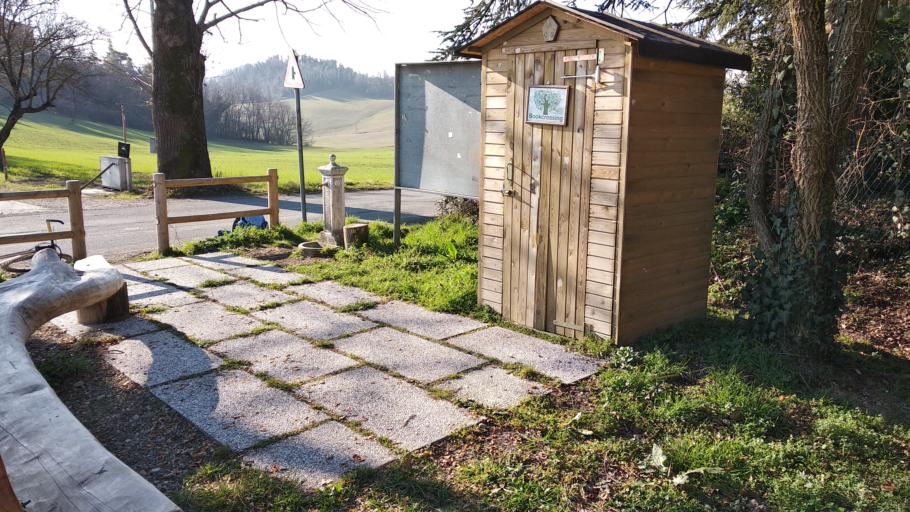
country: IT
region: Emilia-Romagna
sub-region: Provincia di Bologna
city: Ozzano dell'Emilia
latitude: 44.4027
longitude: 11.4600
